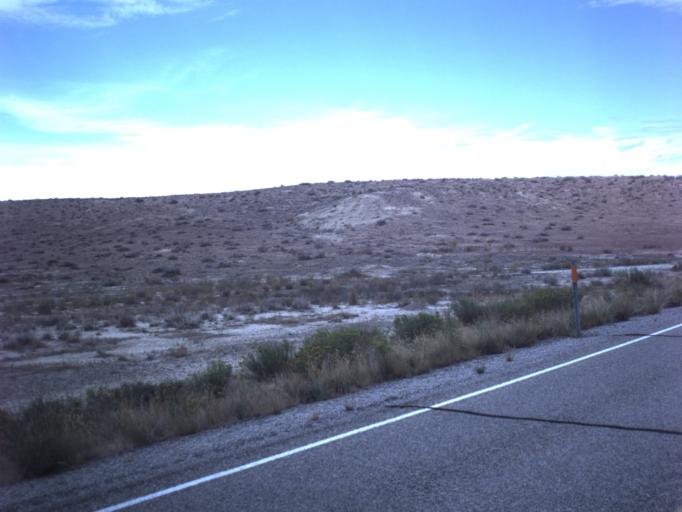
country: US
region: Utah
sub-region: Grand County
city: Moab
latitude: 38.9385
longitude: -109.3482
